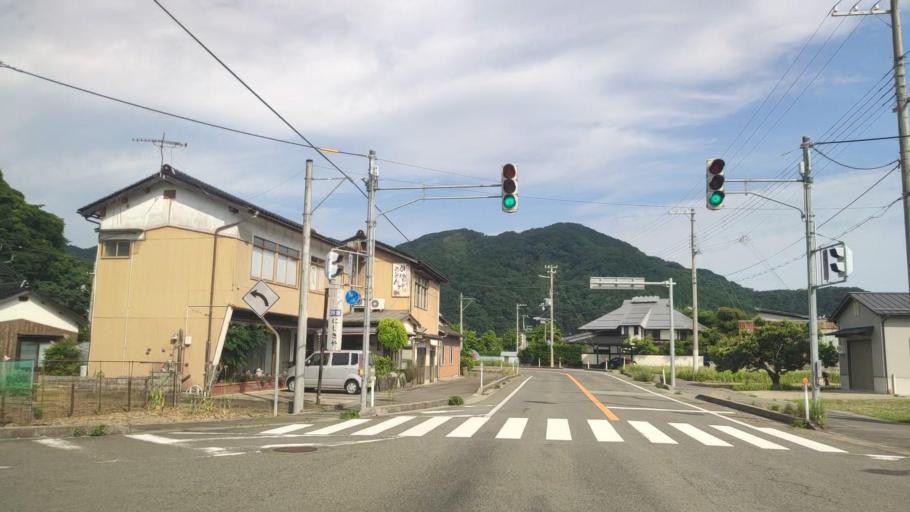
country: JP
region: Hyogo
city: Toyooka
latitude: 35.6424
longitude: 134.8328
